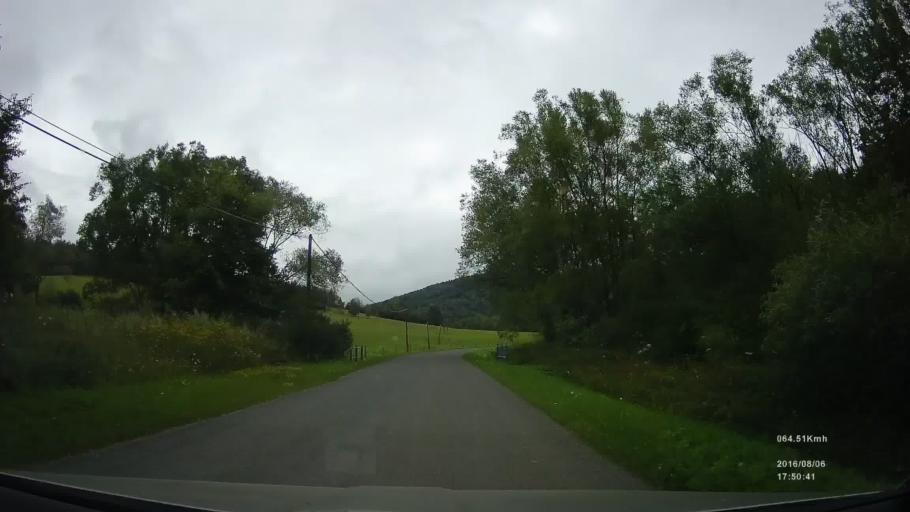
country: SK
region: Presovsky
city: Svidnik
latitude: 49.3945
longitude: 21.5679
